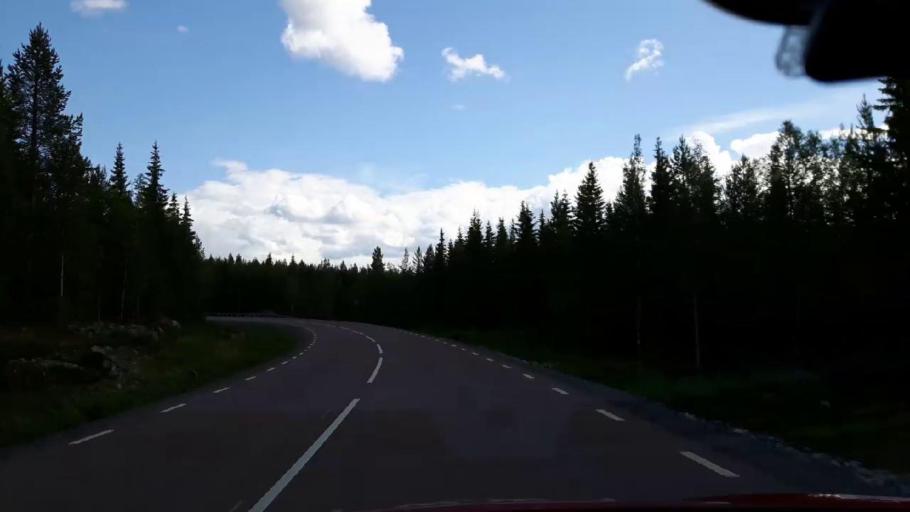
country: SE
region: Jaemtland
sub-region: Krokoms Kommun
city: Valla
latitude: 64.0497
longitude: 14.1717
